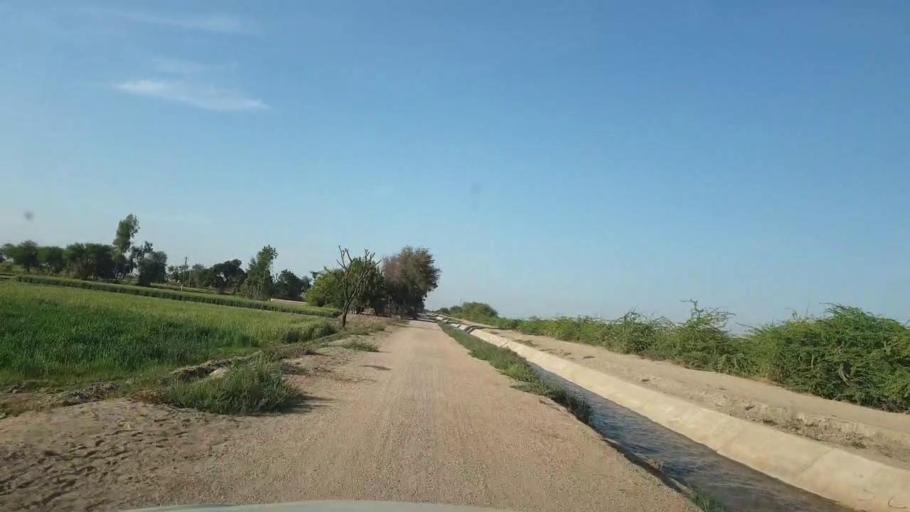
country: PK
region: Sindh
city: Kunri
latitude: 25.0938
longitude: 69.4284
